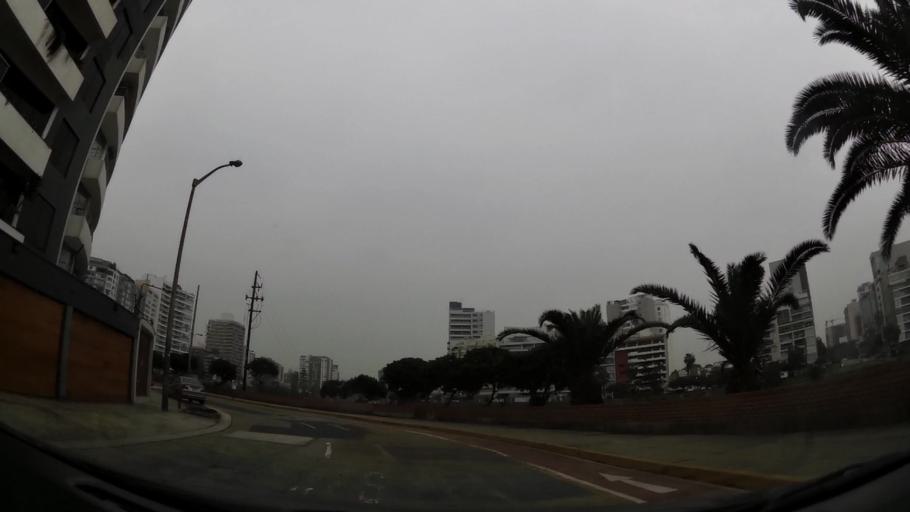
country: PE
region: Lima
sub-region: Lima
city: Surco
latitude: -12.1374
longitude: -77.0272
